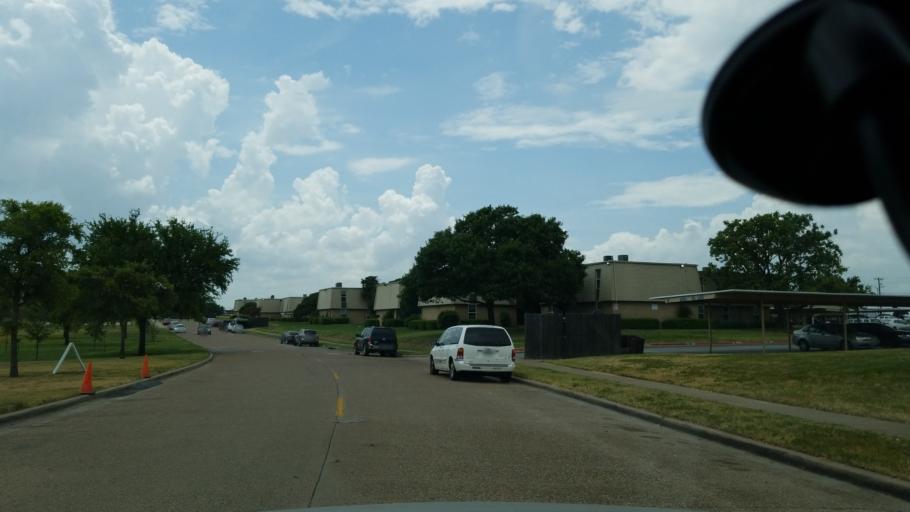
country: US
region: Texas
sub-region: Dallas County
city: Cockrell Hill
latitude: 32.6854
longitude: -96.8552
